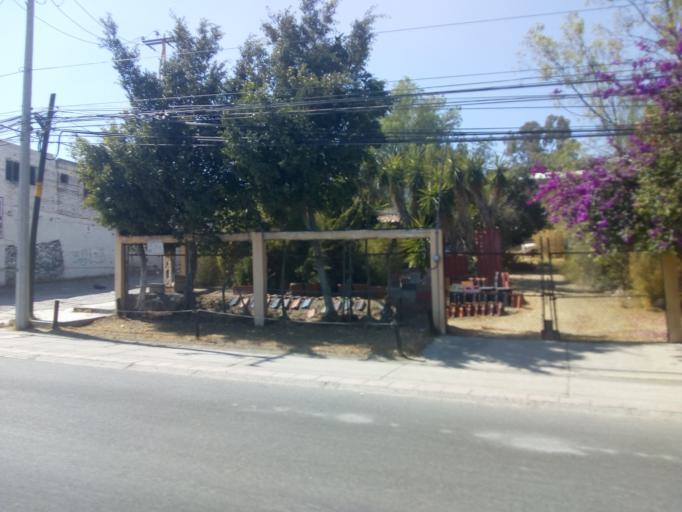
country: MX
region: Guanajuato
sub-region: Leon
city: Centro Familiar la Soledad
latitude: 21.0969
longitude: -101.7262
